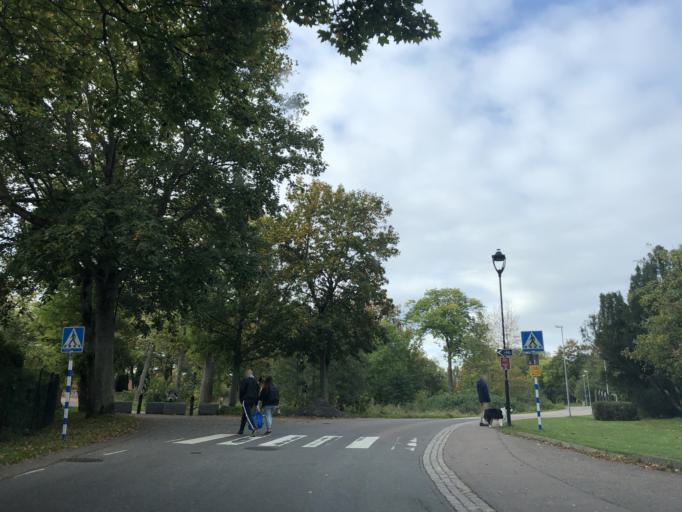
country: SE
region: Vaestra Goetaland
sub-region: Goteborg
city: Majorna
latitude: 57.6822
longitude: 11.8888
